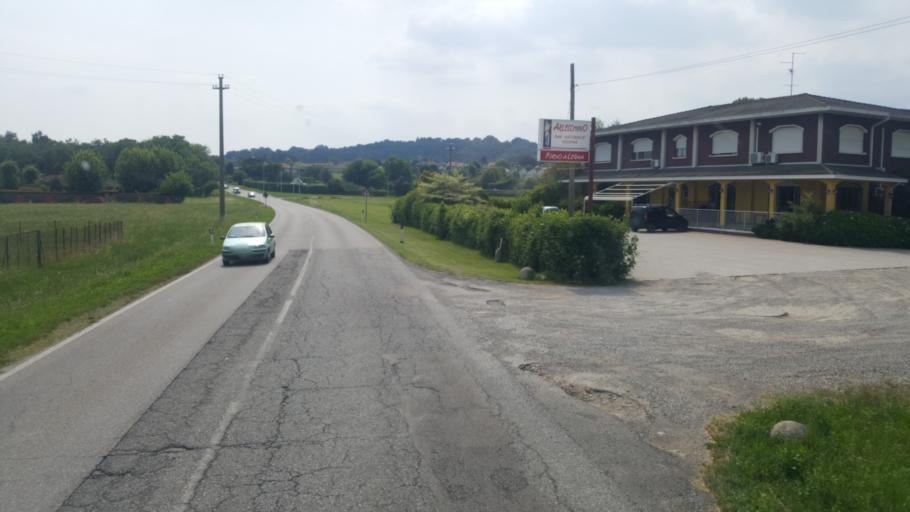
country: IT
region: Lombardy
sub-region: Provincia di Como
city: Lurate Caccivio
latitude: 45.7567
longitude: 8.9917
